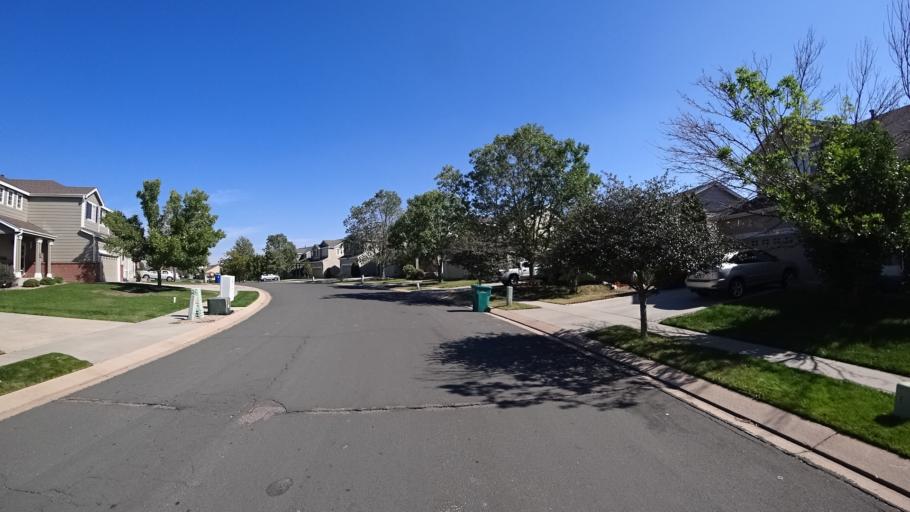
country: US
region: Colorado
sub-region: El Paso County
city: Cimarron Hills
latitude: 38.8854
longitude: -104.6920
